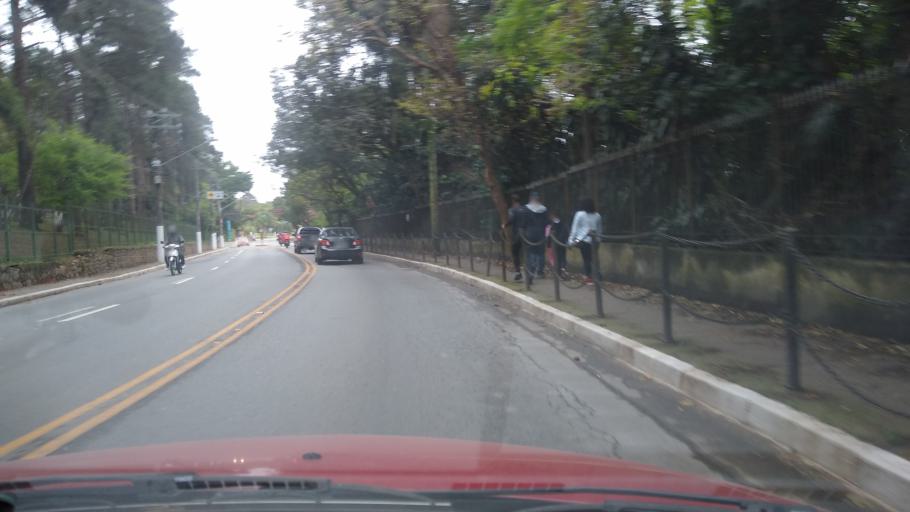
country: BR
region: Sao Paulo
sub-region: Diadema
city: Diadema
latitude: -23.6499
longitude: -46.6216
